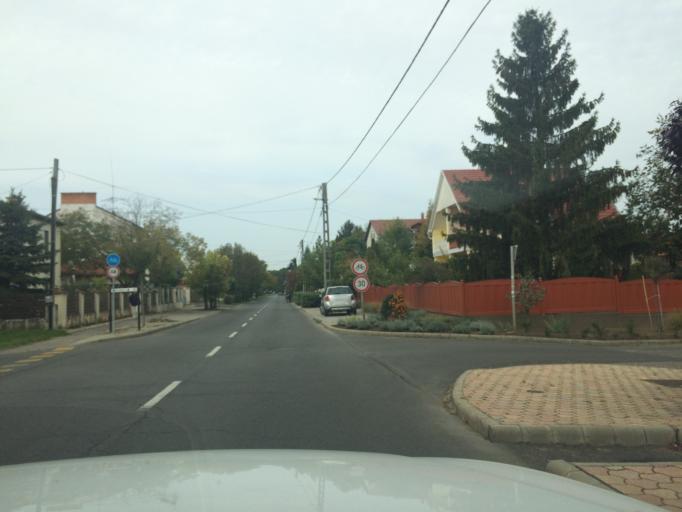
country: HU
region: Szabolcs-Szatmar-Bereg
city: Kotaj
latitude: 48.0087
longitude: 21.7360
